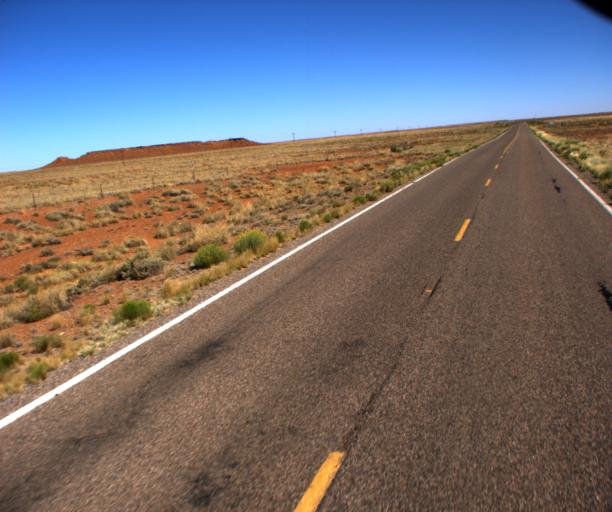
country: US
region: Arizona
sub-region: Coconino County
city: LeChee
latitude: 35.2175
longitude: -110.9521
